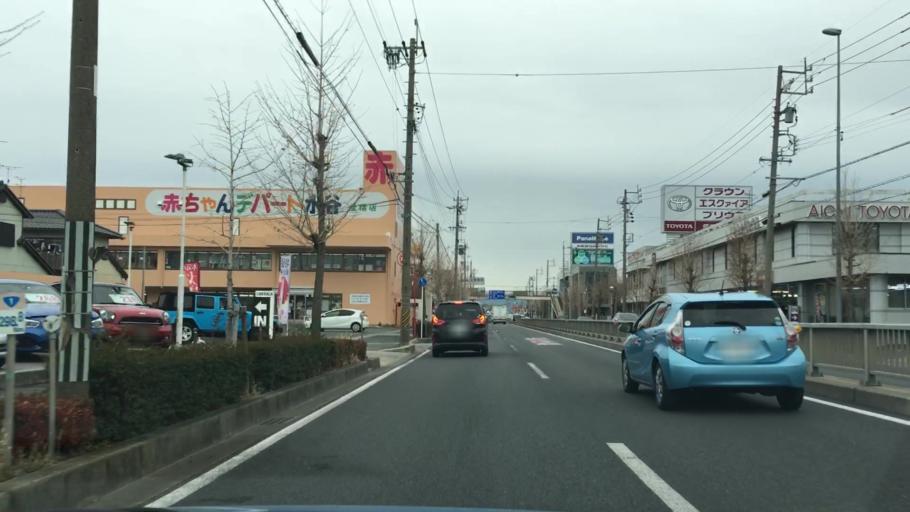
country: JP
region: Aichi
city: Toyohashi
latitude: 34.7852
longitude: 137.3784
